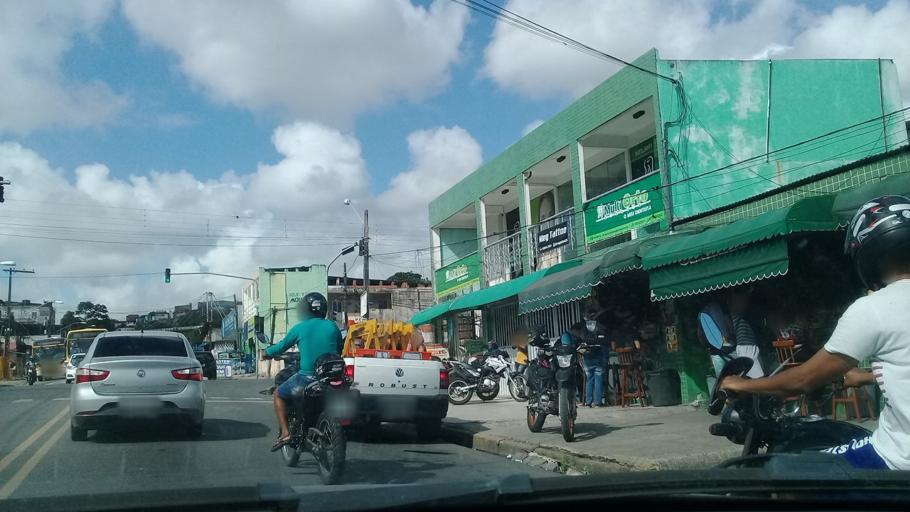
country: BR
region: Pernambuco
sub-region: Jaboatao Dos Guararapes
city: Jaboatao dos Guararapes
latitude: -8.1175
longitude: -34.9417
